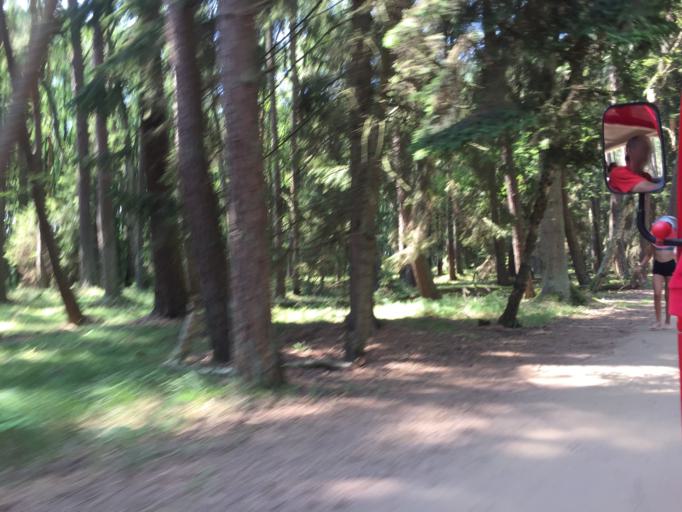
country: PL
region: Pomeranian Voivodeship
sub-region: Powiat leborski
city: Leba
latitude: 54.7486
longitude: 17.4511
